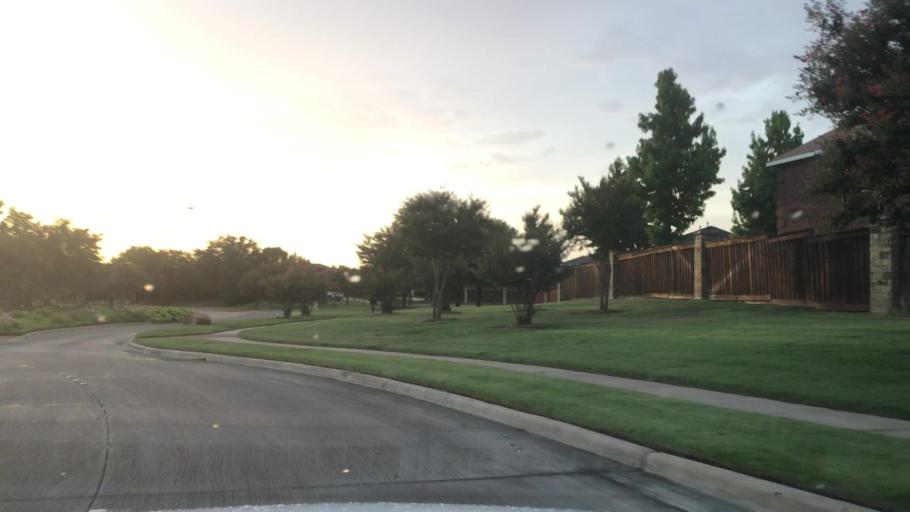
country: US
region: Texas
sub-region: Kaufman County
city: Forney
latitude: 32.7184
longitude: -96.5358
